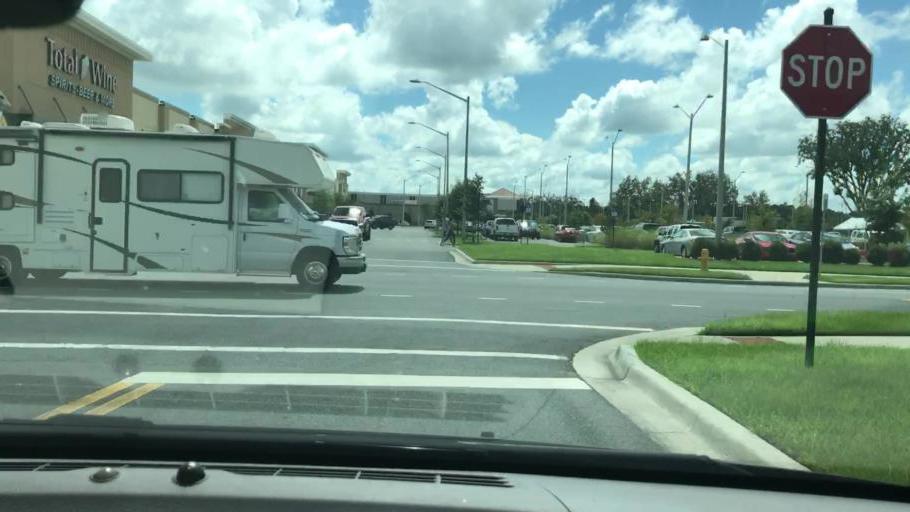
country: US
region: Florida
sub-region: Alachua County
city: Gainesville
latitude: 29.6281
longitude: -82.3834
